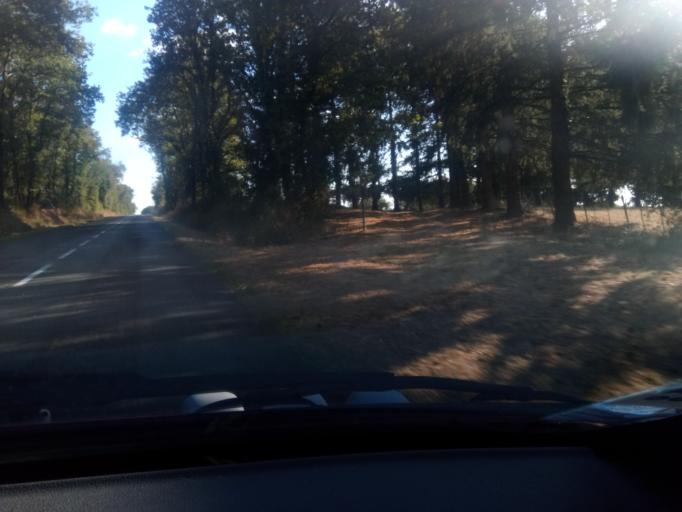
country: FR
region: Poitou-Charentes
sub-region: Departement de la Vienne
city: Lussac-les-Chateaux
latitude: 46.3298
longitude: 0.7090
